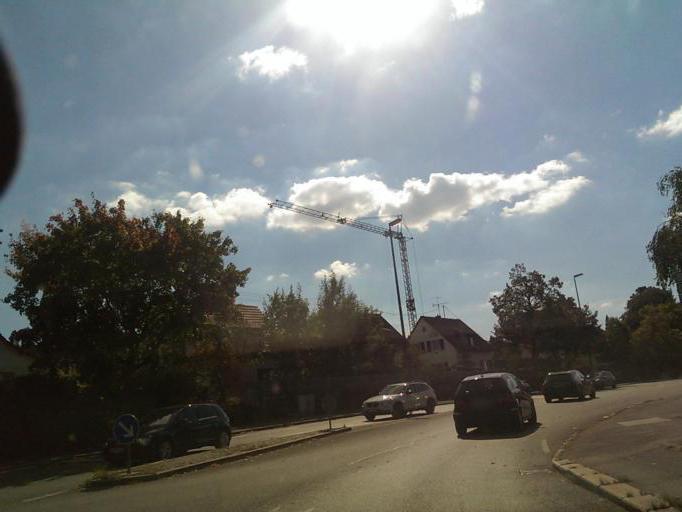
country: DE
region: Baden-Wuerttemberg
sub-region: Regierungsbezirk Stuttgart
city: Sindelfingen
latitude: 48.7013
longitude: 9.0082
